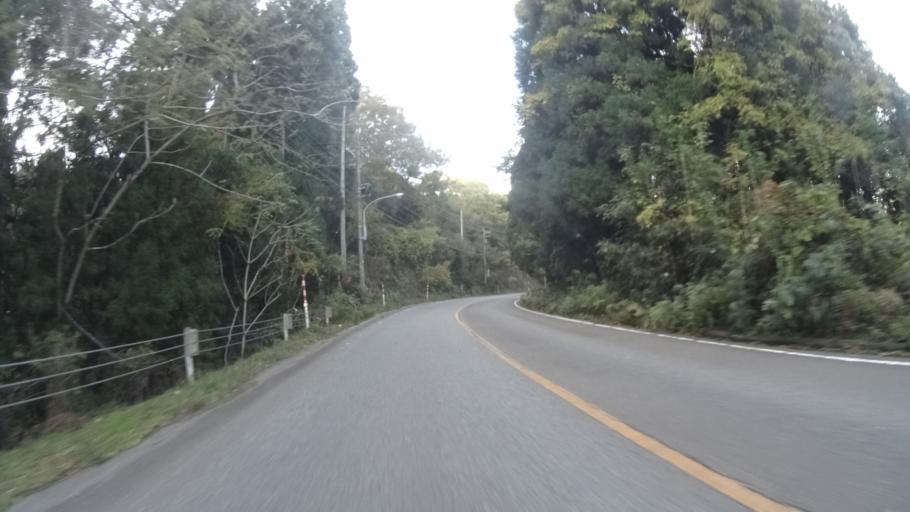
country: JP
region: Ishikawa
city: Nanao
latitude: 37.1798
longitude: 136.7132
